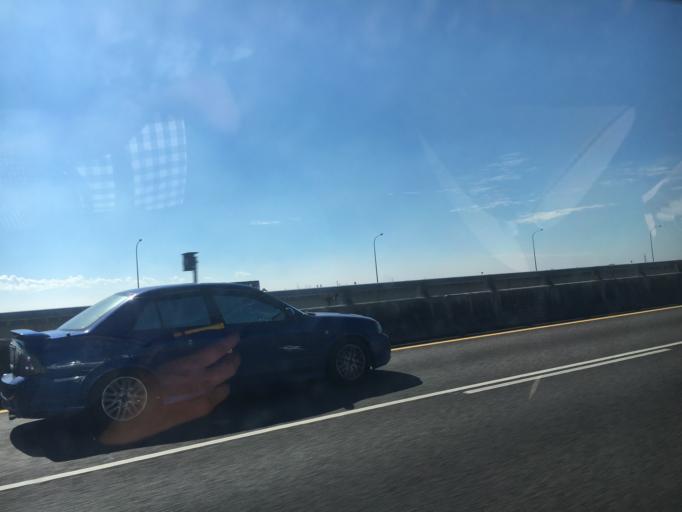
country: TW
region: Taiwan
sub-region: Taoyuan
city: Taoyuan
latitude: 25.0654
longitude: 121.3583
